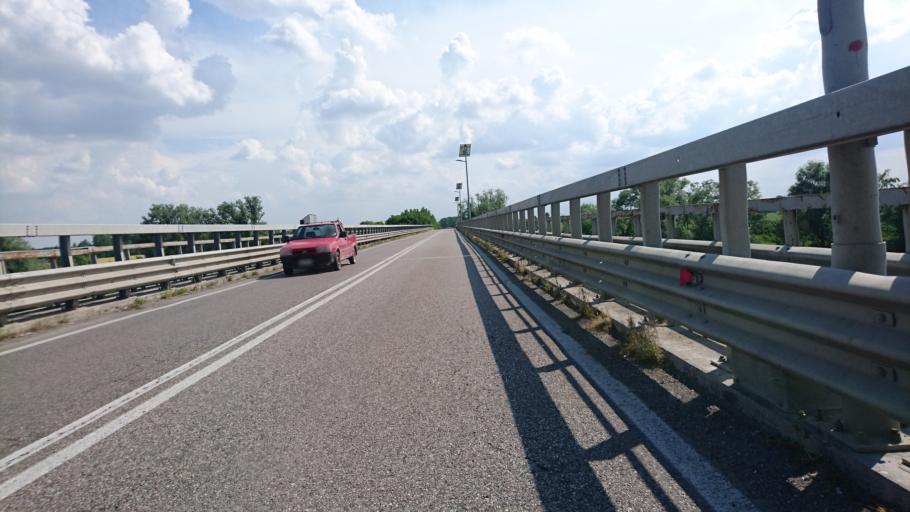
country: IT
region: Lombardy
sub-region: Provincia di Mantova
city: Sermide
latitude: 45.0146
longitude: 11.2895
